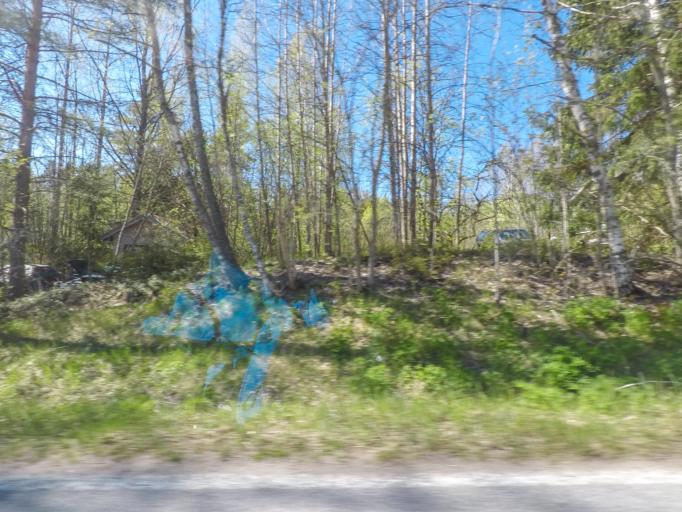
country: FI
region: Uusimaa
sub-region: Helsinki
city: Sammatti
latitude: 60.3509
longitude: 23.7999
